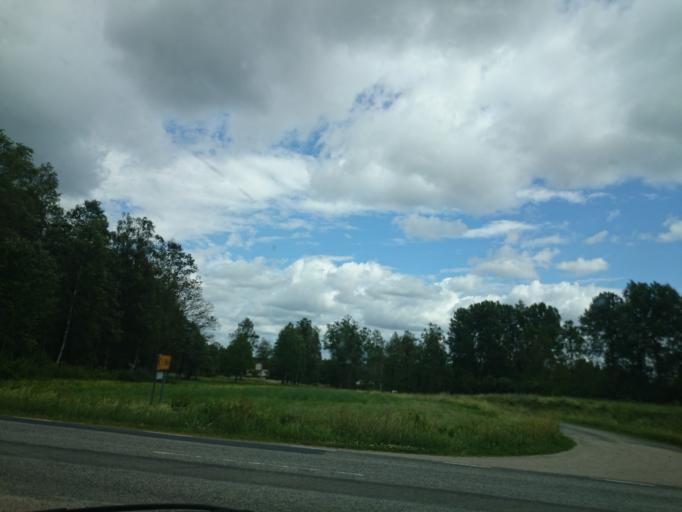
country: SE
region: Joenkoeping
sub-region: Varnamo Kommun
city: Forsheda
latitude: 57.0748
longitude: 13.9393
